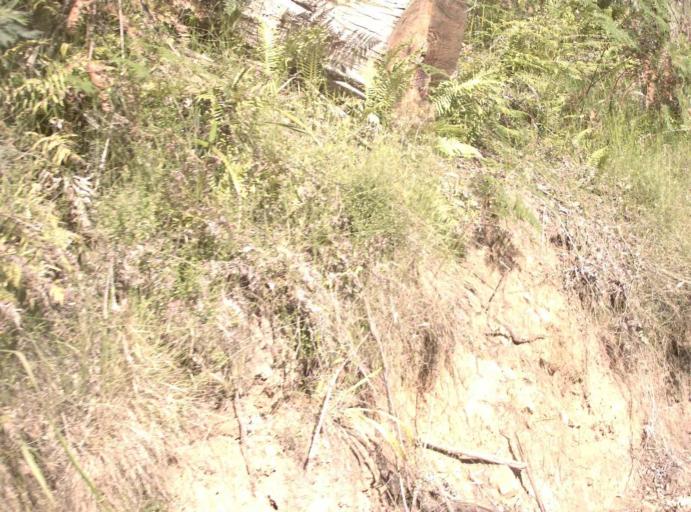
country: AU
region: Victoria
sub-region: East Gippsland
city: Lakes Entrance
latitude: -37.4099
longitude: 148.5938
